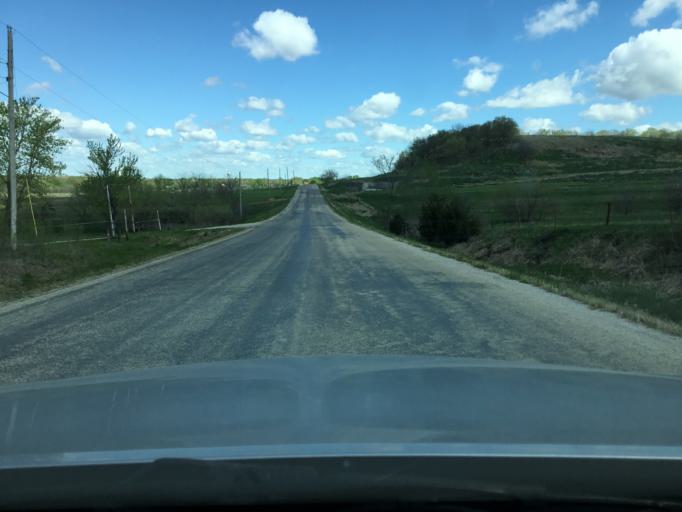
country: US
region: Kansas
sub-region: Anderson County
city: Garnett
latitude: 38.3517
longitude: -95.1253
